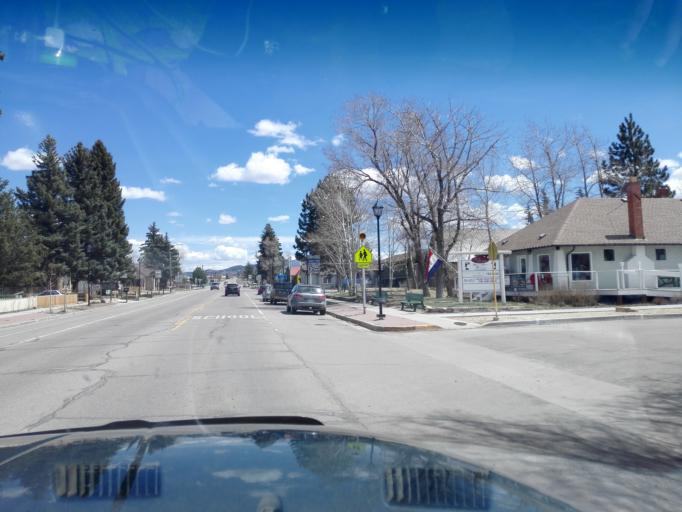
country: US
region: Colorado
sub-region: Custer County
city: Westcliffe
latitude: 38.1360
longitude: -105.4651
